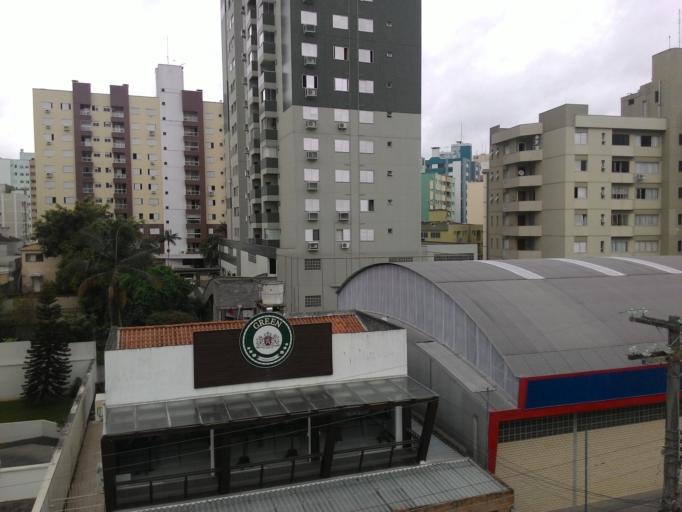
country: BR
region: Santa Catarina
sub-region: Criciuma
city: Criciuma
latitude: -28.6811
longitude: -49.3724
